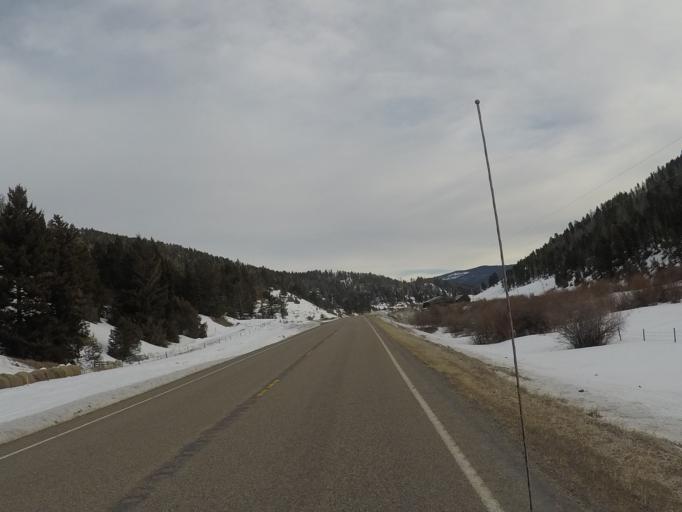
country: US
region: Montana
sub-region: Meagher County
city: White Sulphur Springs
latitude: 46.6845
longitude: -110.8744
